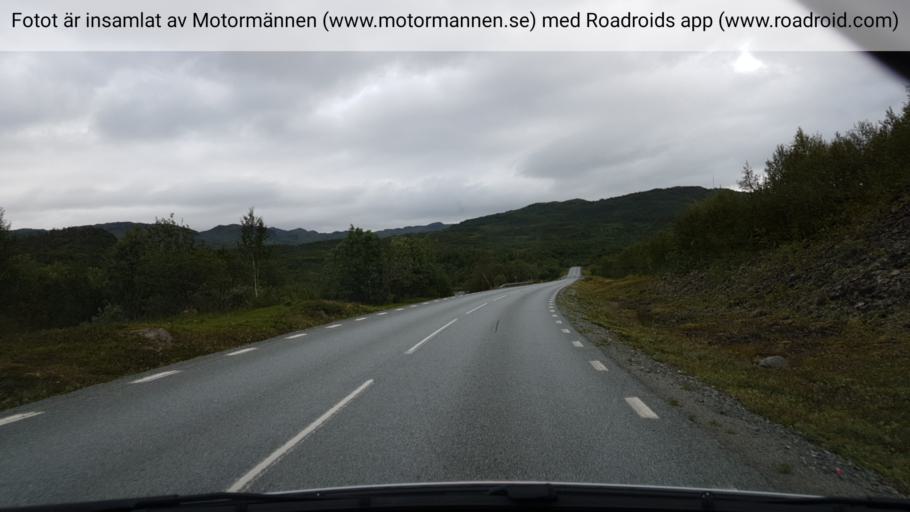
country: NO
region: Nordland
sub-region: Rana
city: Mo i Rana
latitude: 66.1280
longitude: 14.6309
